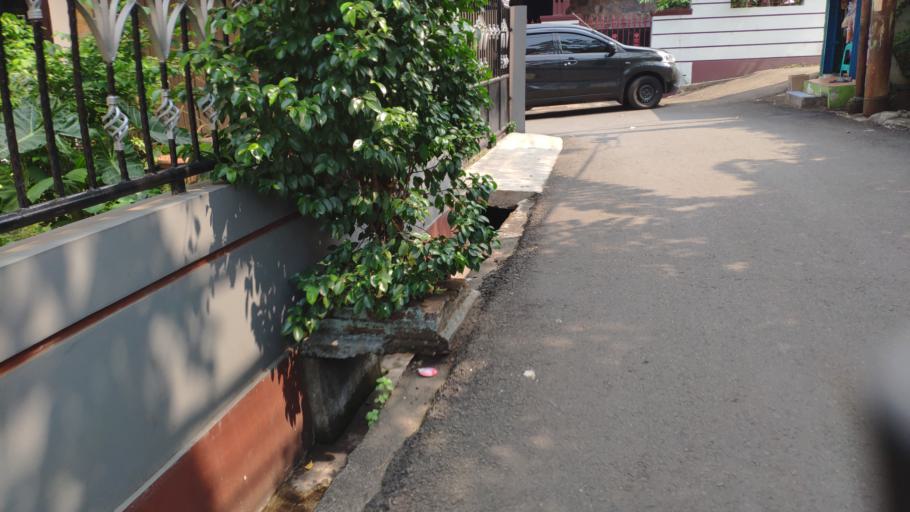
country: ID
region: Jakarta Raya
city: Jakarta
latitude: -6.3052
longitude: 106.8285
